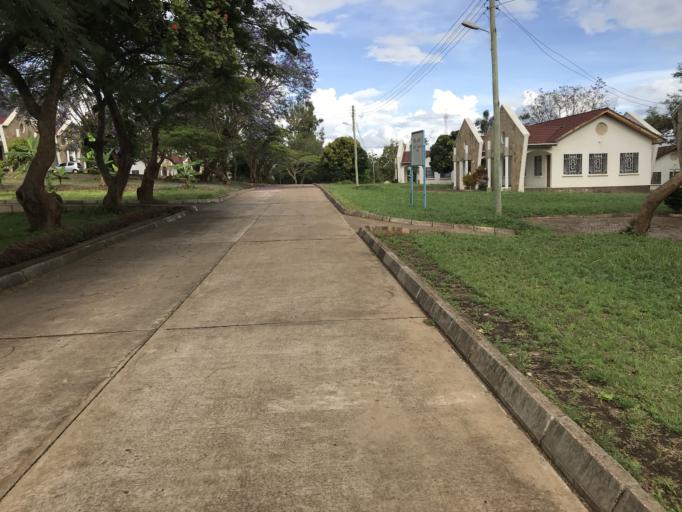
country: TZ
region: Arusha
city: Usa River
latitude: -3.3999
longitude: 36.7992
